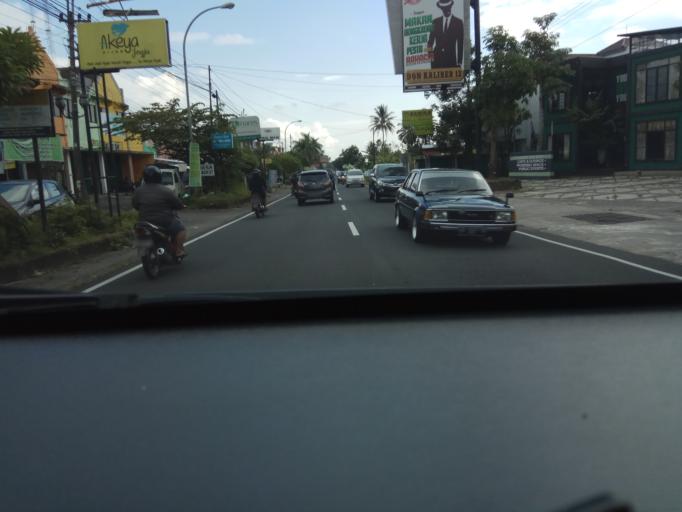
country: ID
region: Daerah Istimewa Yogyakarta
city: Melati
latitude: -7.7075
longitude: 110.4109
